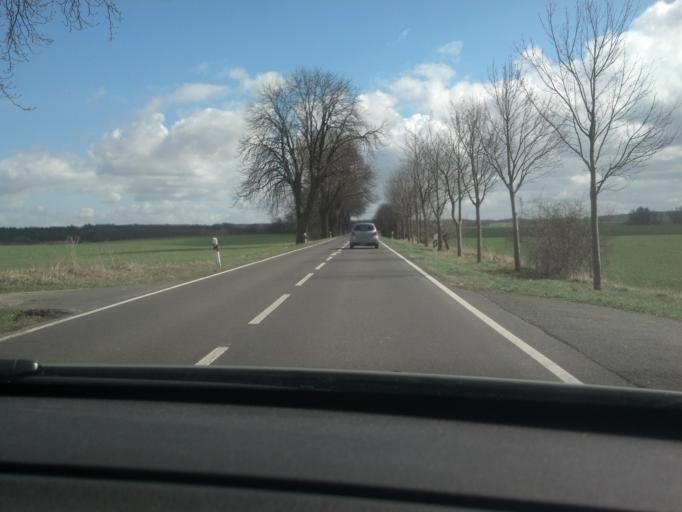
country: DE
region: Mecklenburg-Vorpommern
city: Loitz
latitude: 53.3664
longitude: 13.3759
